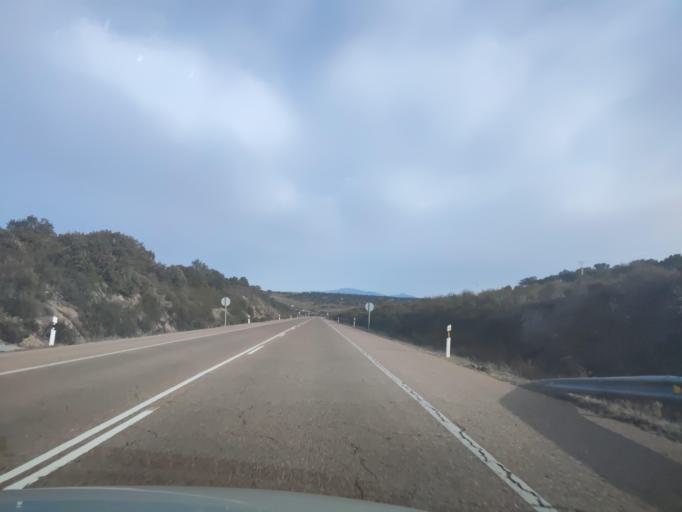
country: ES
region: Castille and Leon
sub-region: Provincia de Salamanca
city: Carpio de Azaba
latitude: 40.5910
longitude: -6.6791
